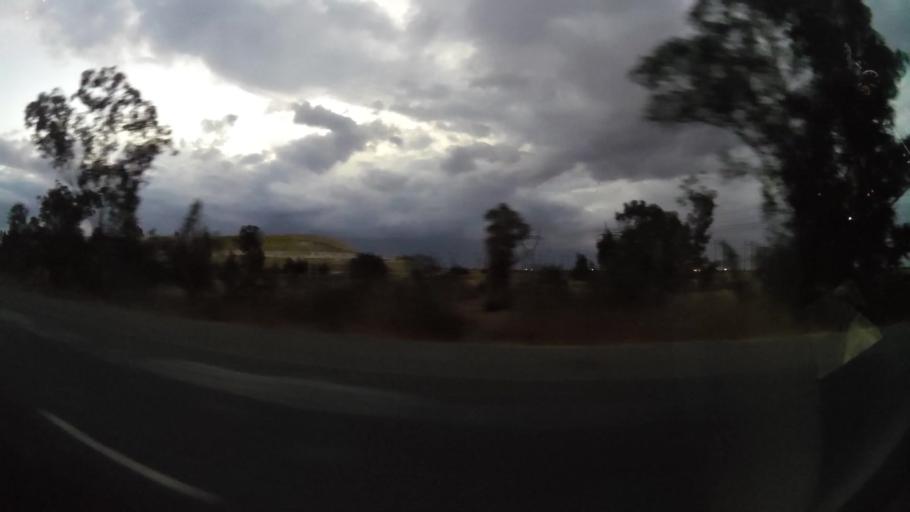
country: ZA
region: Orange Free State
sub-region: Lejweleputswa District Municipality
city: Welkom
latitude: -27.9330
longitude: 26.7858
